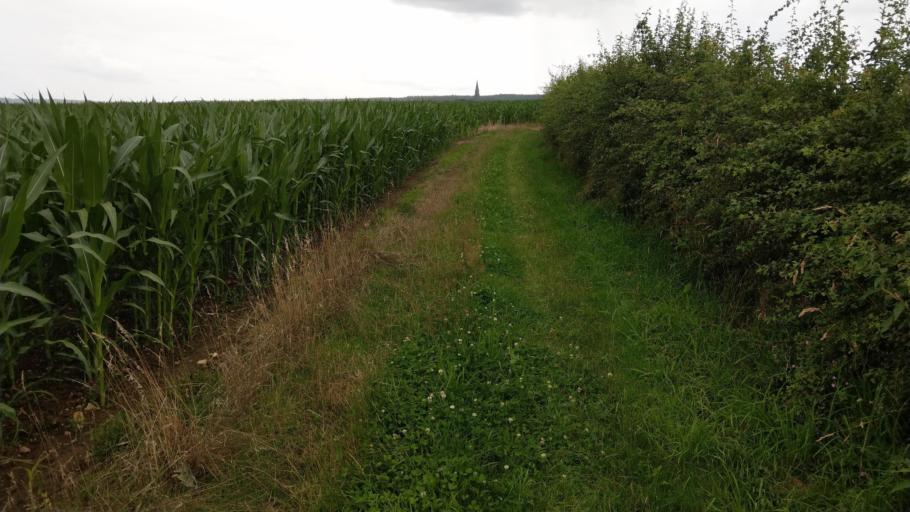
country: NL
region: Limburg
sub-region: Gemeente Simpelveld
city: Simpelveld
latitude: 50.7997
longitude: 5.9614
